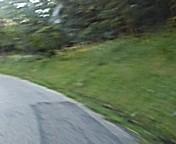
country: FR
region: Rhone-Alpes
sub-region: Departement de l'Isere
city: Saint-Egreve
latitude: 45.2811
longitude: 5.7103
